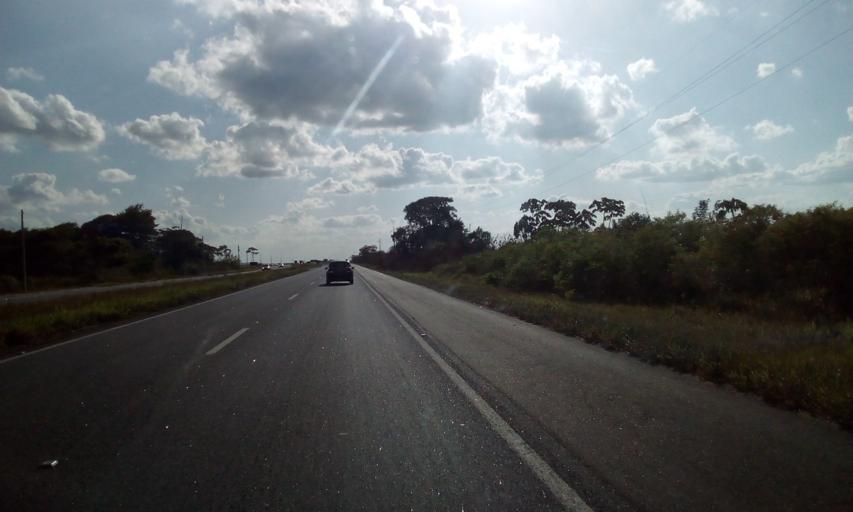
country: BR
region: Paraiba
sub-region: Cruz Do Espirito Santo
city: Cruz do Espirito Santo
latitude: -7.1772
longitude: -35.0442
